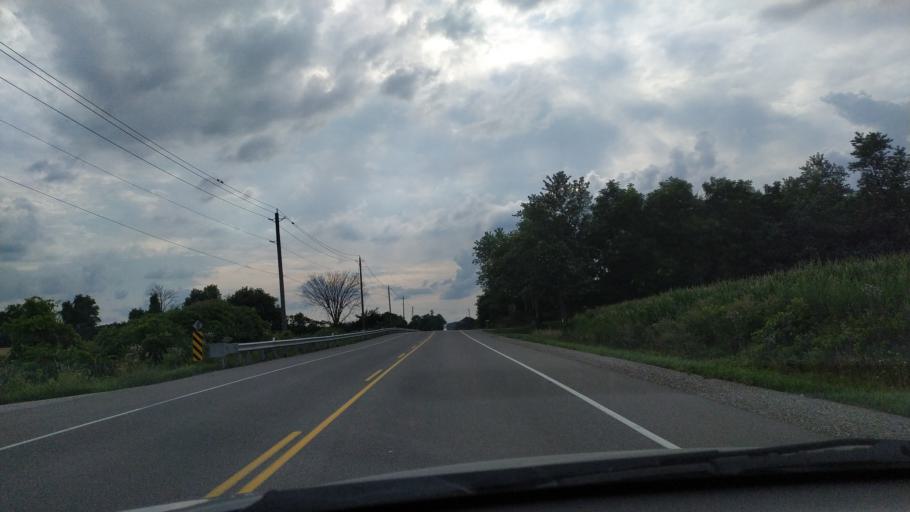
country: CA
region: Ontario
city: Kitchener
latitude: 43.3606
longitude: -80.4665
